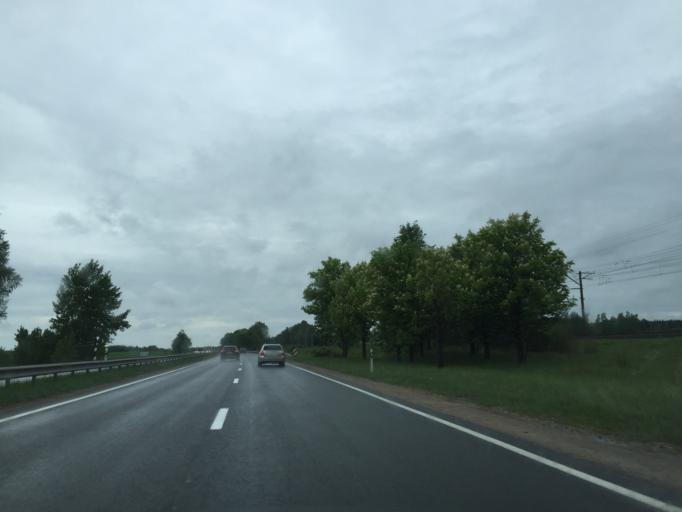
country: LV
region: Ikskile
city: Ikskile
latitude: 56.8467
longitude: 24.4619
